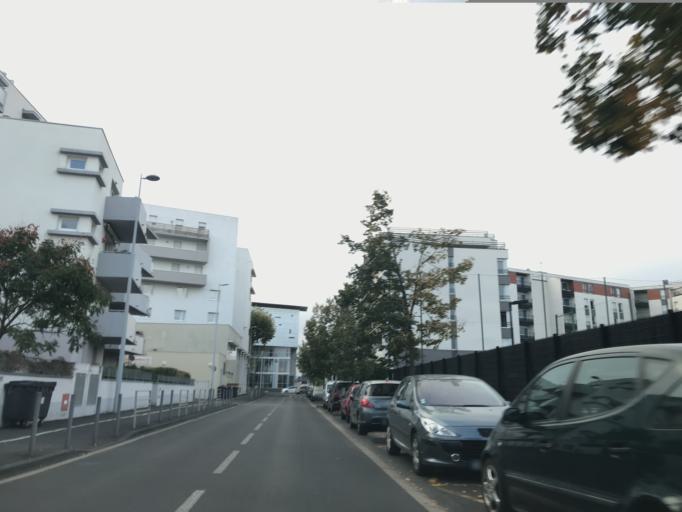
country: FR
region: Auvergne
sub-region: Departement du Puy-de-Dome
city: Clermont-Ferrand
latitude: 45.7899
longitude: 3.1080
